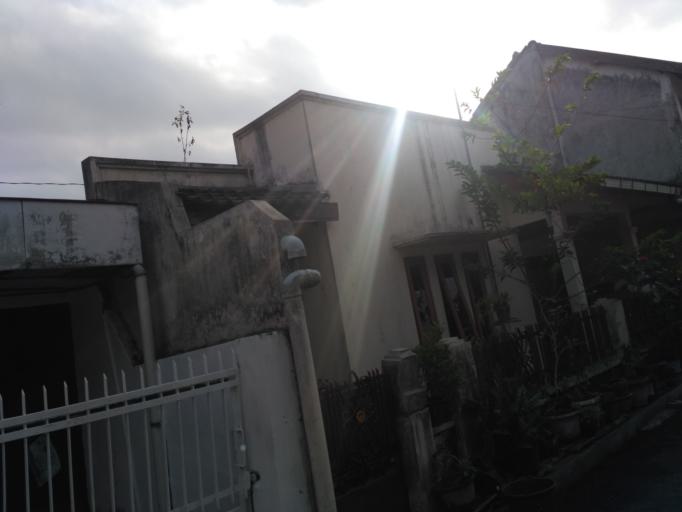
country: ID
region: Daerah Istimewa Yogyakarta
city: Melati
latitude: -7.7369
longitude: 110.3863
